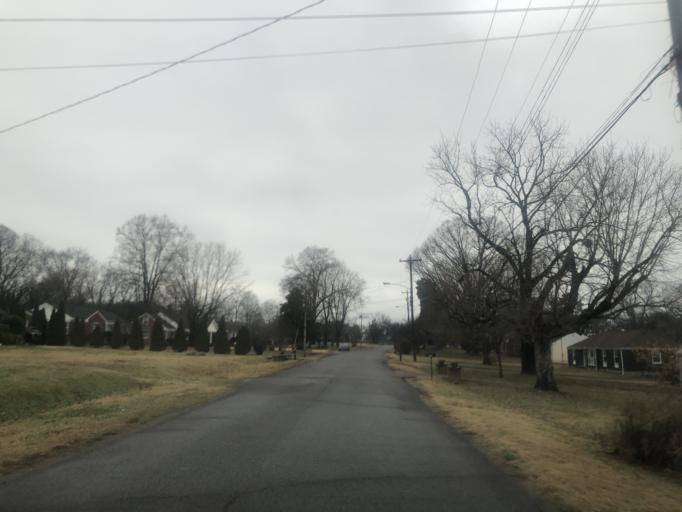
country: US
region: Tennessee
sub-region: Davidson County
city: Lakewood
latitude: 36.1673
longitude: -86.6837
